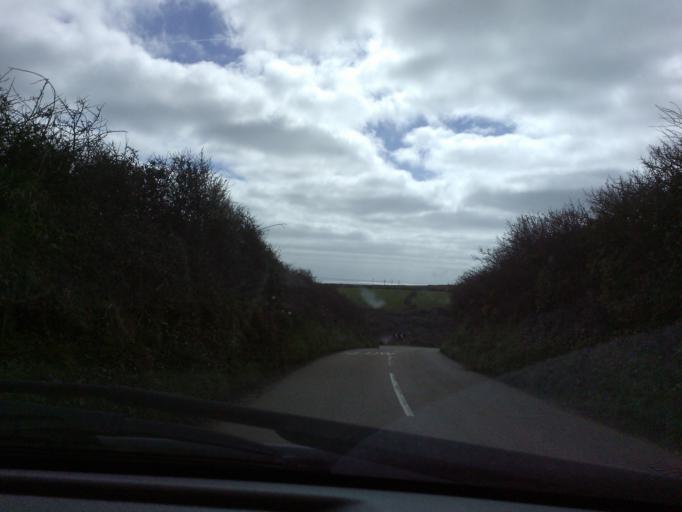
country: GB
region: England
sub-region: Cornwall
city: St. Buryan
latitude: 50.0546
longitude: -5.6373
